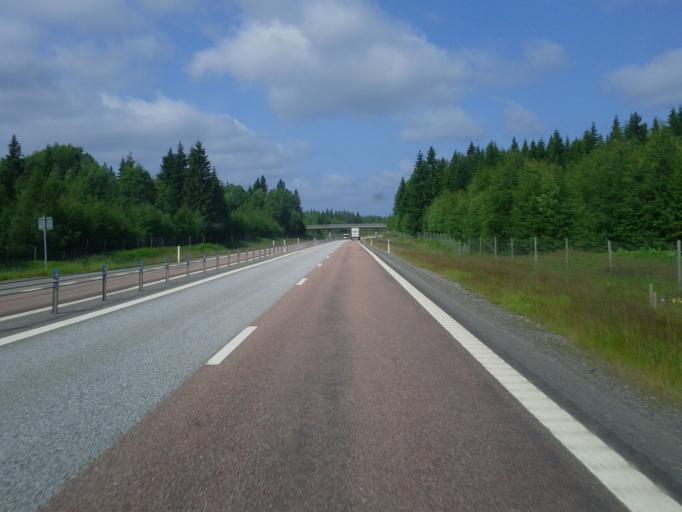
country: SE
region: Vaesterbotten
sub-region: Skelleftea Kommun
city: Soedra Bergsbyn
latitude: 64.6951
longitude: 21.0203
